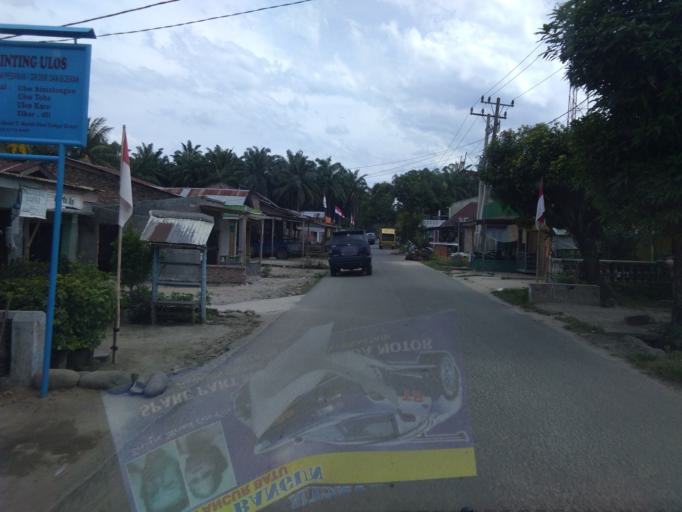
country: ID
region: North Sumatra
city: Deli Tua
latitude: 3.2995
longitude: 98.8080
